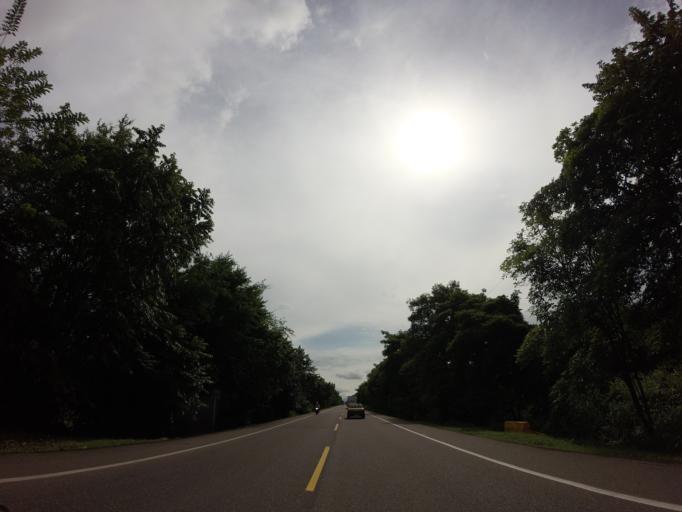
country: CO
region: Caldas
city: La Dorada
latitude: 5.3805
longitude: -74.7123
